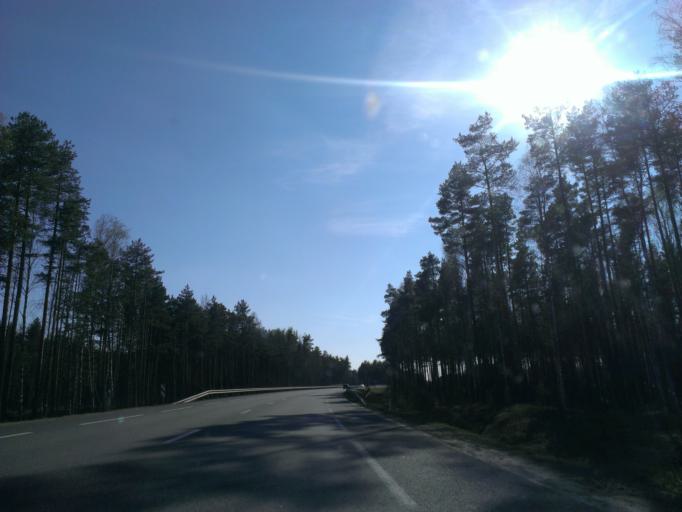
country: LV
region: Saulkrastu
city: Saulkrasti
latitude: 57.1971
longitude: 24.3690
